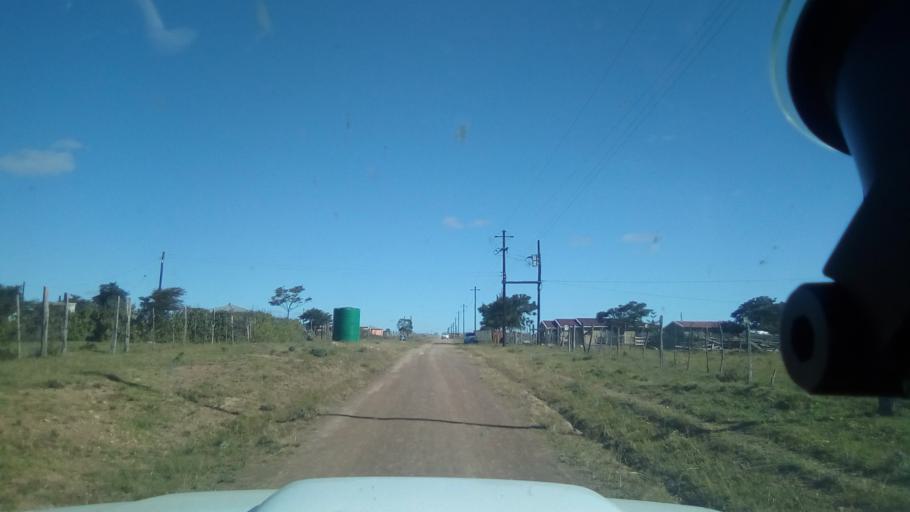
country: ZA
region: Eastern Cape
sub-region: Buffalo City Metropolitan Municipality
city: Bhisho
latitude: -32.7830
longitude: 27.3341
